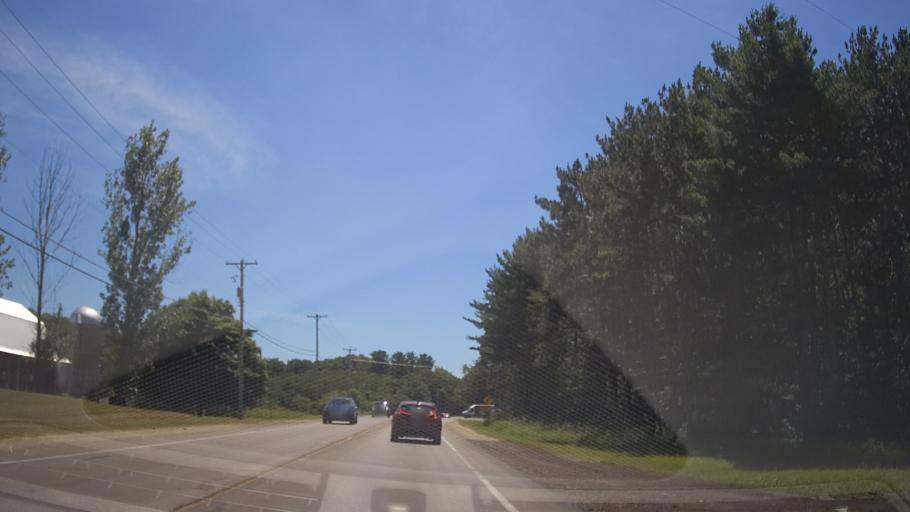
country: US
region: Michigan
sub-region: Grand Traverse County
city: Traverse City
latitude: 44.7172
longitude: -85.6850
